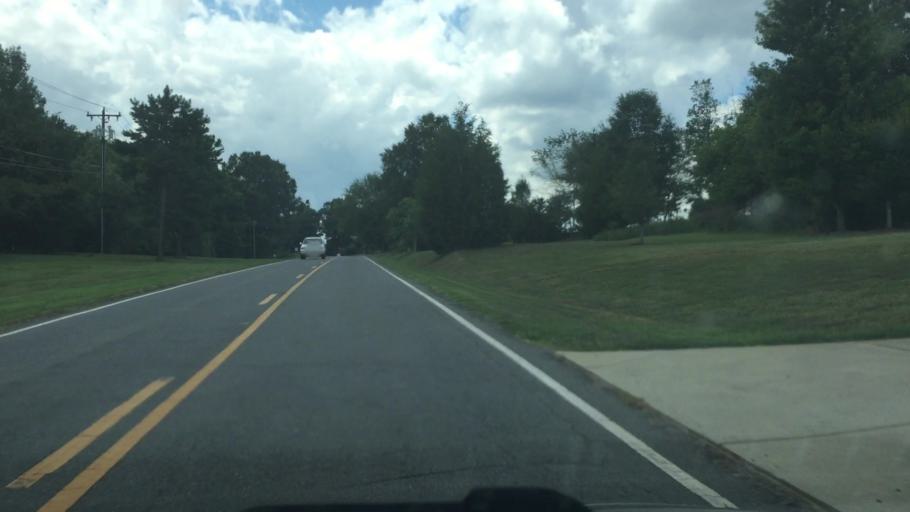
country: US
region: North Carolina
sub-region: Rowan County
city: Enochville
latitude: 35.4629
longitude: -80.7315
